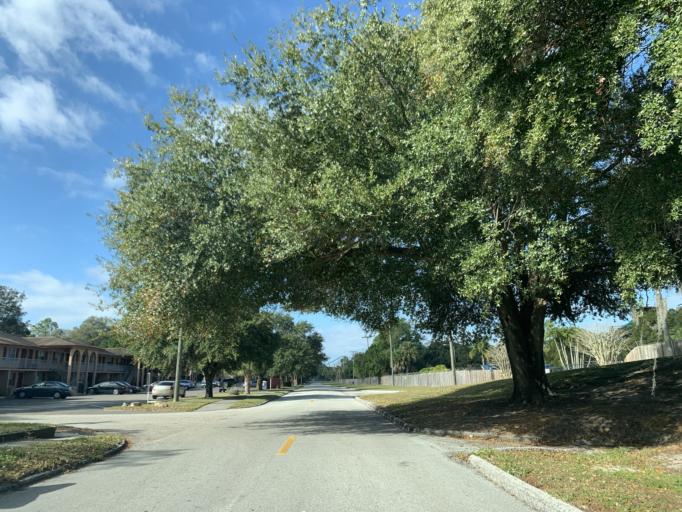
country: US
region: Florida
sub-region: Hillsborough County
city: Temple Terrace
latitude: 28.0399
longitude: -82.4118
